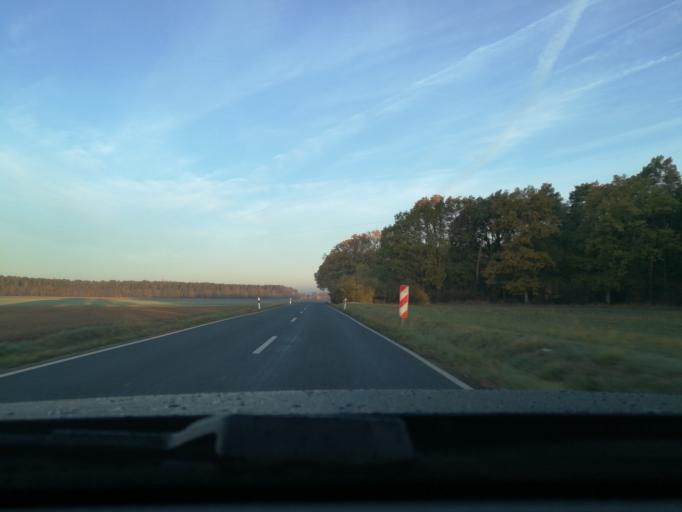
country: DE
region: Bavaria
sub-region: Regierungsbezirk Mittelfranken
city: Obermichelbach
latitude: 49.5412
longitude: 10.9347
